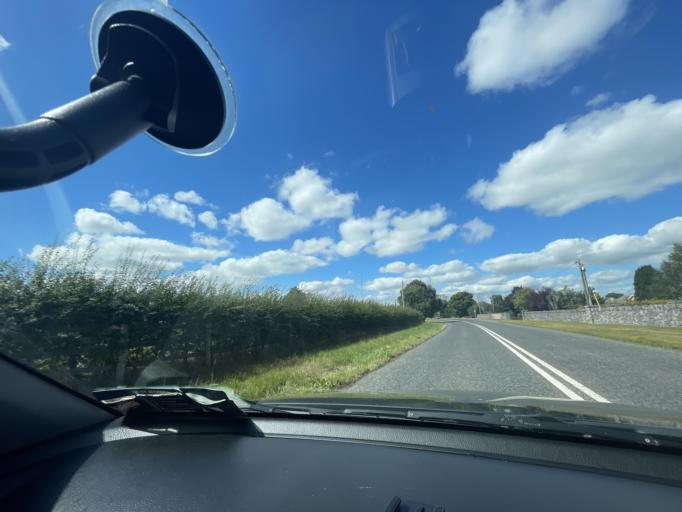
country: IE
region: Leinster
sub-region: An Mhi
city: Newtown Trim
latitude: 53.5279
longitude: -6.6786
